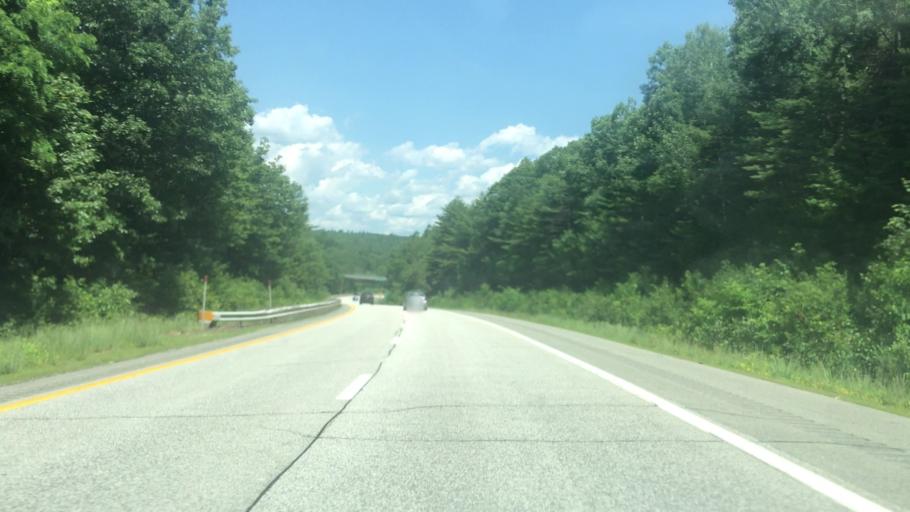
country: US
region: New Hampshire
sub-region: Merrimack County
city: Henniker
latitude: 43.2708
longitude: -71.7969
